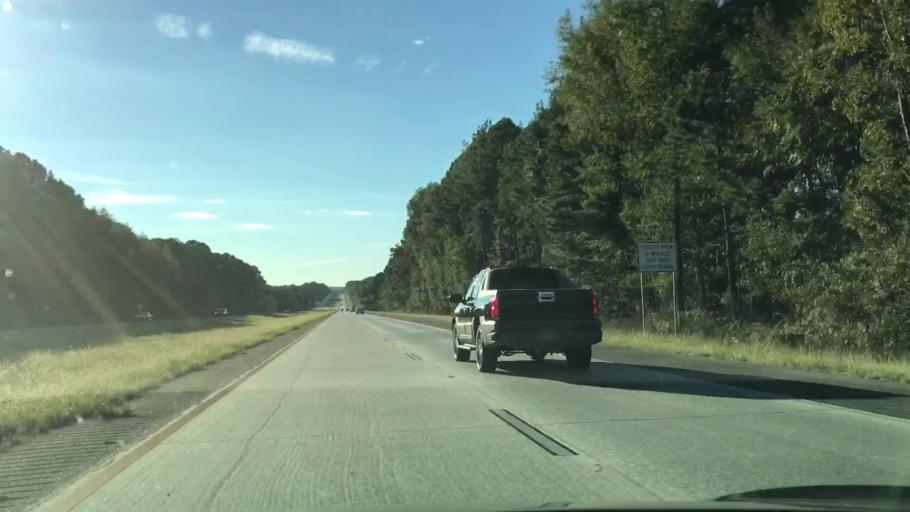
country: US
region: Georgia
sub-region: Greene County
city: Union Point
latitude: 33.5453
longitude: -83.0912
